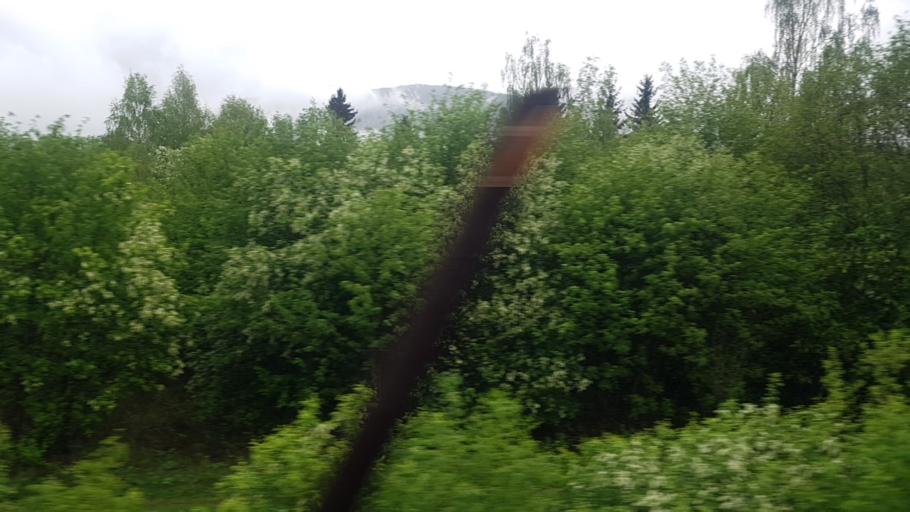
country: NO
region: Oppland
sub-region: Ringebu
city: Ringebu
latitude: 61.4398
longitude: 10.2064
